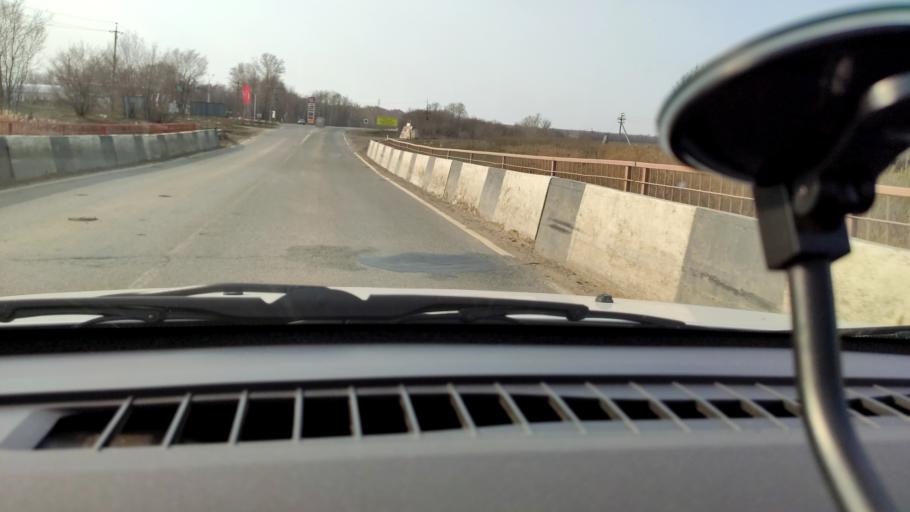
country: RU
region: Samara
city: Dubovyy Umet
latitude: 53.0652
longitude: 50.3709
